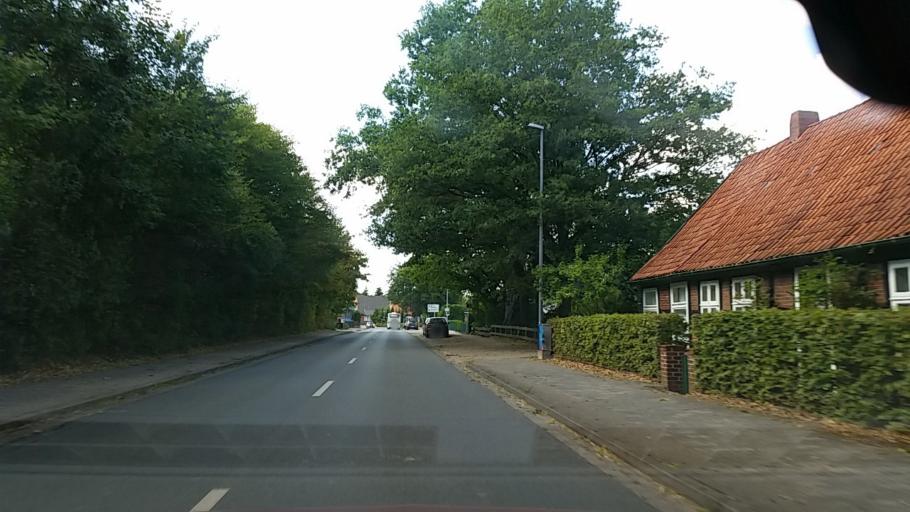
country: DE
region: Lower Saxony
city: Scharnebeck
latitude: 53.2908
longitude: 10.4999
